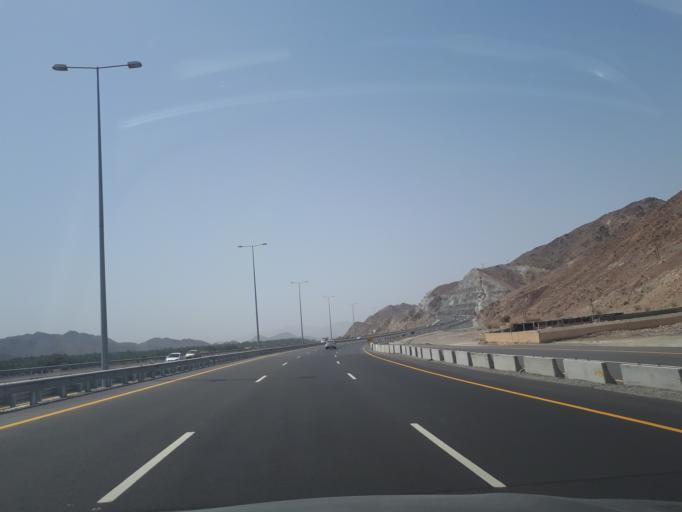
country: OM
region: Muhafazat ad Dakhiliyah
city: Bidbid
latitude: 23.3791
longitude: 58.1037
